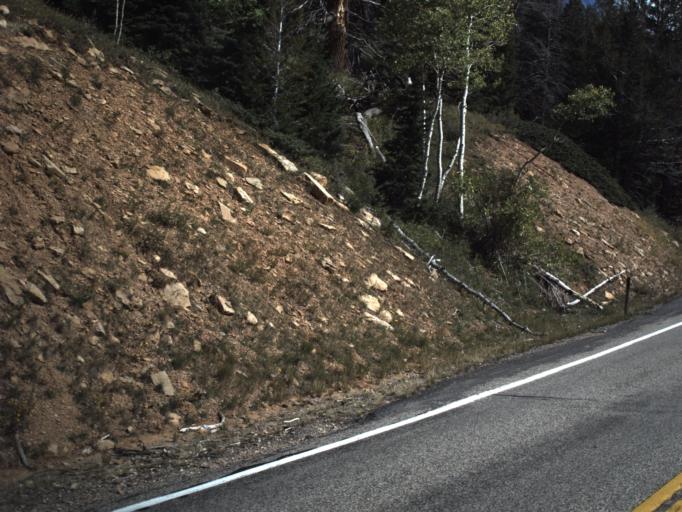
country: US
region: Utah
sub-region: Iron County
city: Cedar City
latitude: 37.5795
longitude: -112.8717
